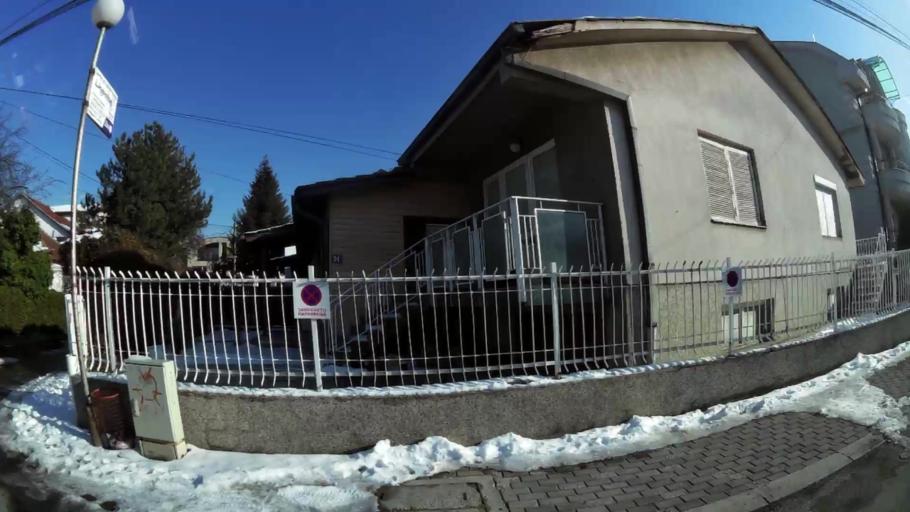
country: MK
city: Krushopek
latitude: 42.0024
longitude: 21.3802
